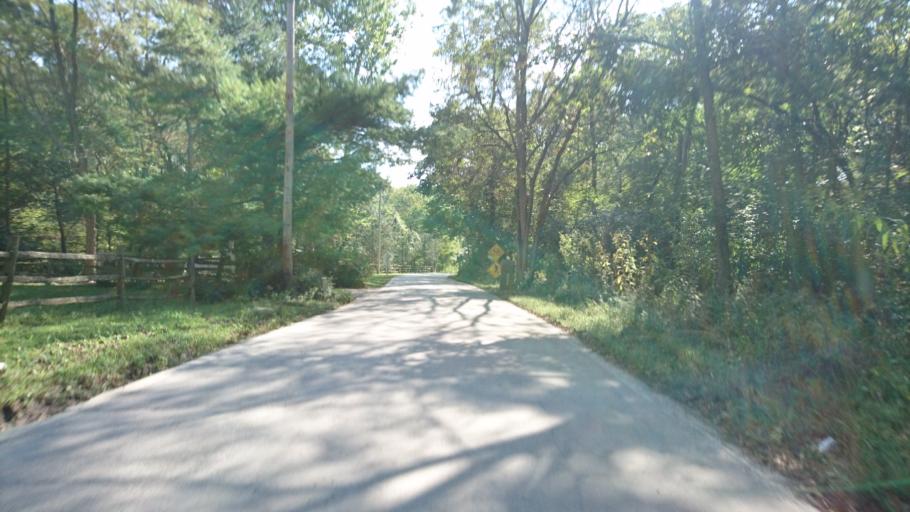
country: US
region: Missouri
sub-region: Saint Louis County
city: Wildwood
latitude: 38.5578
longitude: -90.6419
